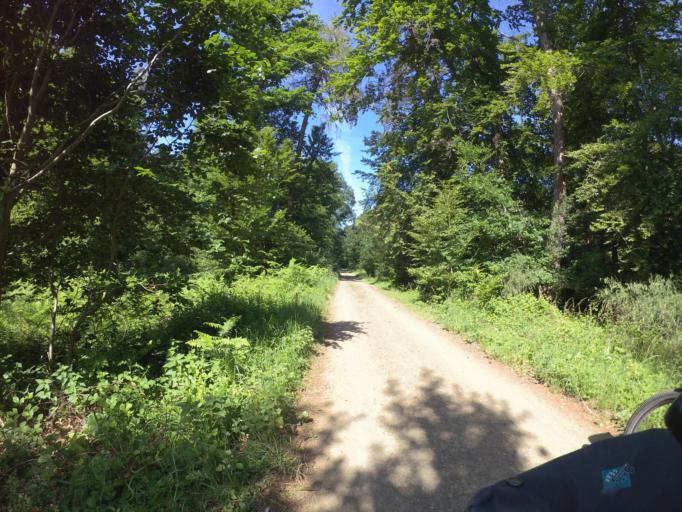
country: DE
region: Rheinland-Pfalz
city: Waldmohr
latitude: 49.3734
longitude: 7.3068
